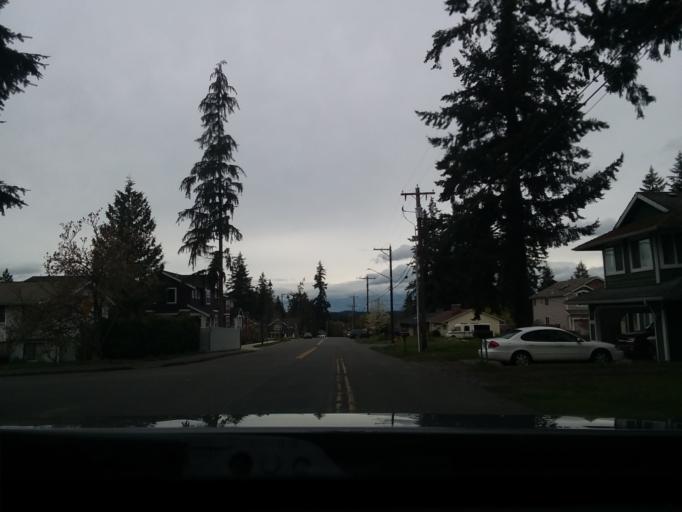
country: US
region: Washington
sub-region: Snohomish County
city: Mountlake Terrace
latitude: 47.8005
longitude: -122.3085
